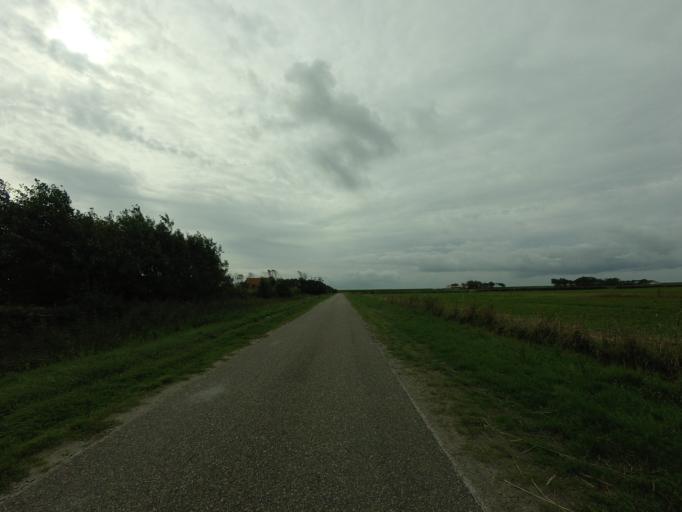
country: NL
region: Friesland
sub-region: Gemeente Ameland
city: Nes
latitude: 53.4373
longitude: 5.7068
